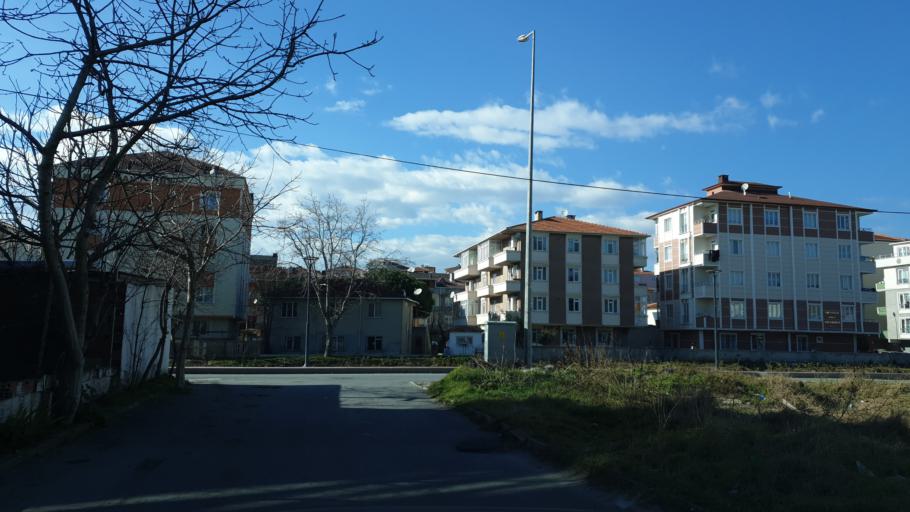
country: TR
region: Tekirdag
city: Cerkezkoey
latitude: 41.2866
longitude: 28.0063
